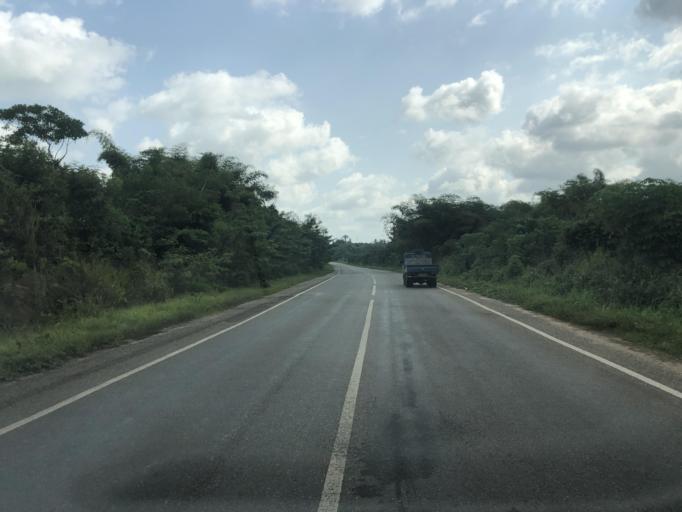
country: GH
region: Central
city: Elmina
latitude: 5.2235
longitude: -1.3242
